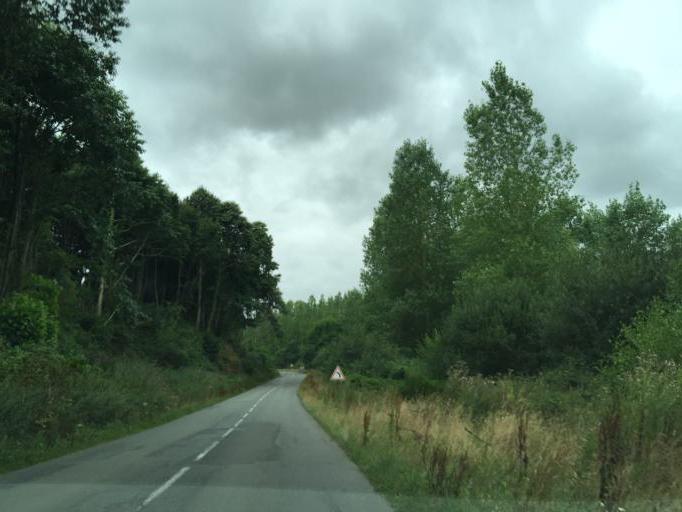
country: FR
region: Brittany
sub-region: Departement des Cotes-d'Armor
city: Jugon-les-Lacs
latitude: 48.4040
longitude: -2.3300
